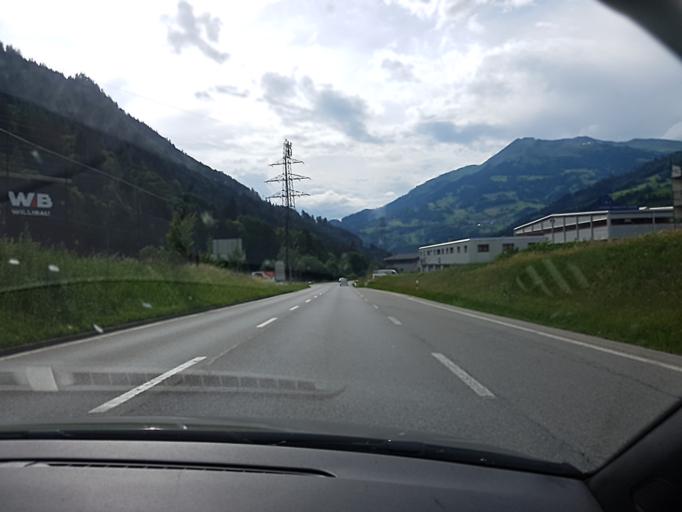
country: CH
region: Grisons
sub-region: Praettigau/Davos District
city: Schiers
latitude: 46.9665
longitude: 9.6888
